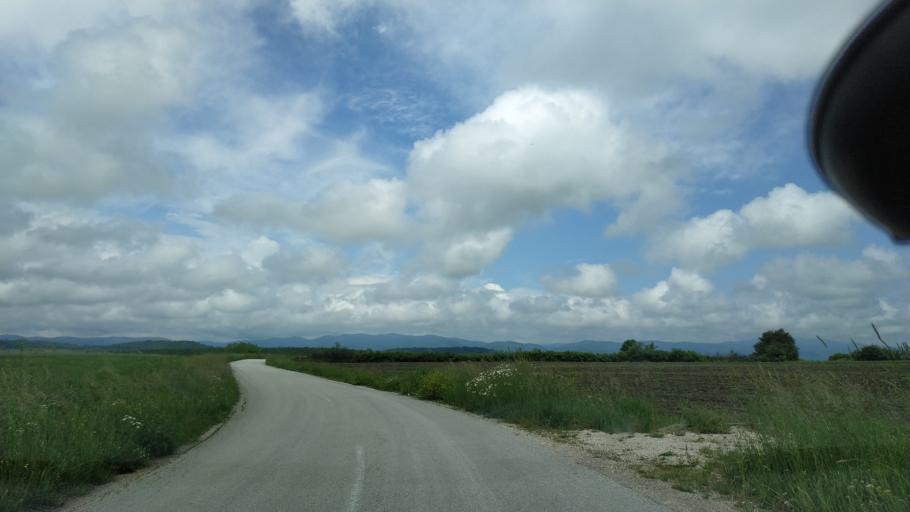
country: RS
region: Central Serbia
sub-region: Zajecarski Okrug
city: Boljevac
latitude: 43.8126
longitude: 21.9549
